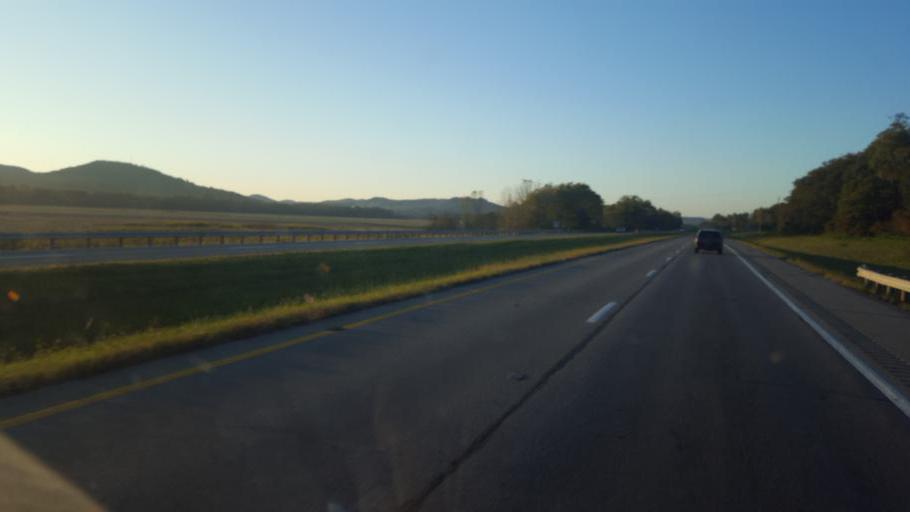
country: US
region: Ohio
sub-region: Scioto County
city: Lucasville
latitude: 38.9079
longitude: -83.0091
